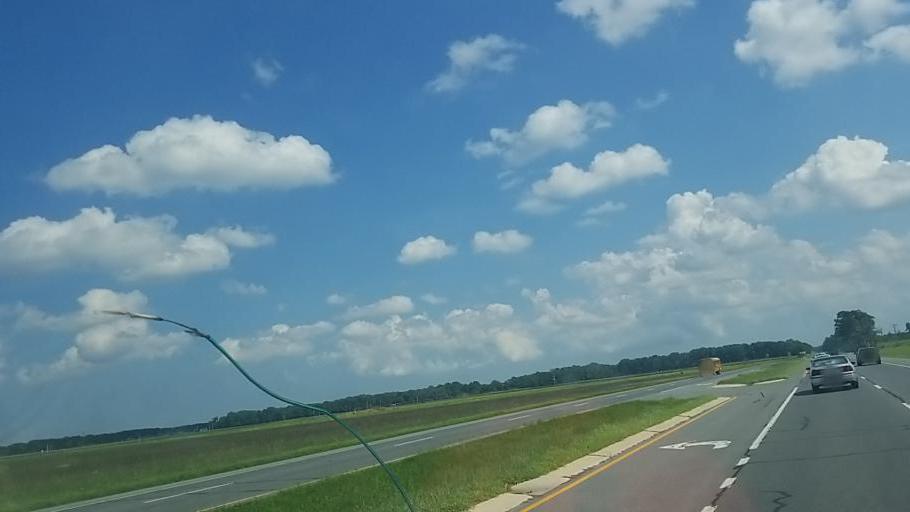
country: US
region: Delaware
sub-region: Sussex County
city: Millsboro
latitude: 38.6232
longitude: -75.3400
